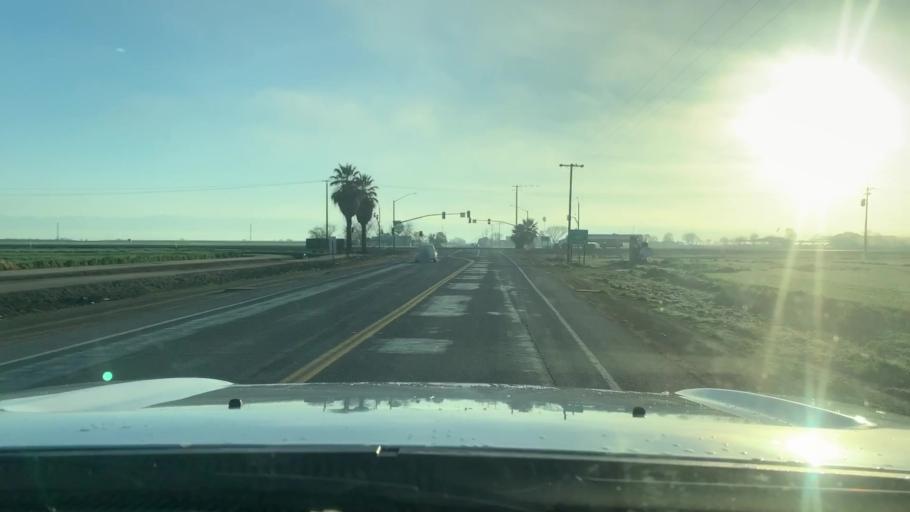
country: US
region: California
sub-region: Kings County
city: Home Garden
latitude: 36.2109
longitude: -119.6023
